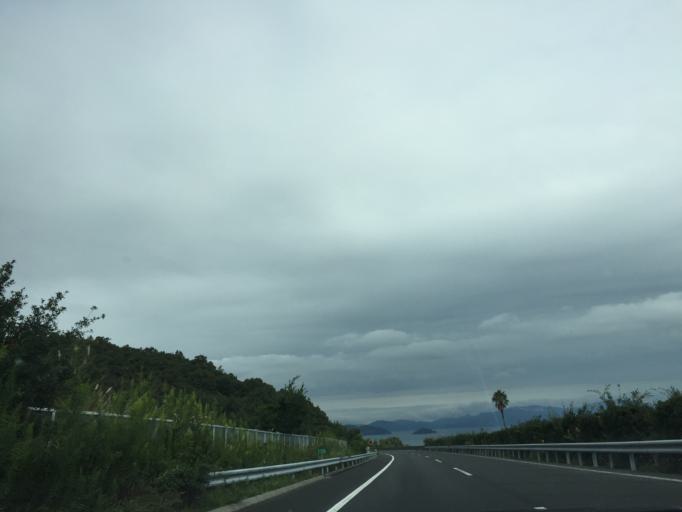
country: JP
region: Kagawa
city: Shido
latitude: 34.2695
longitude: 134.2858
